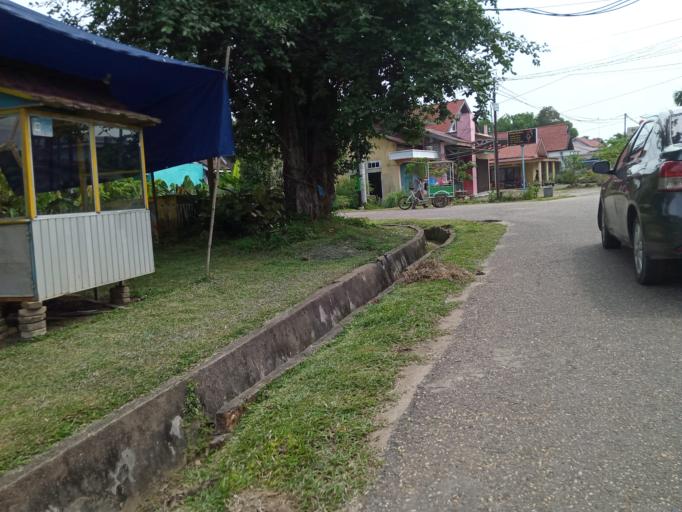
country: ID
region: Jambi
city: Muara Bulian
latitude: -1.7109
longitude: 103.2602
